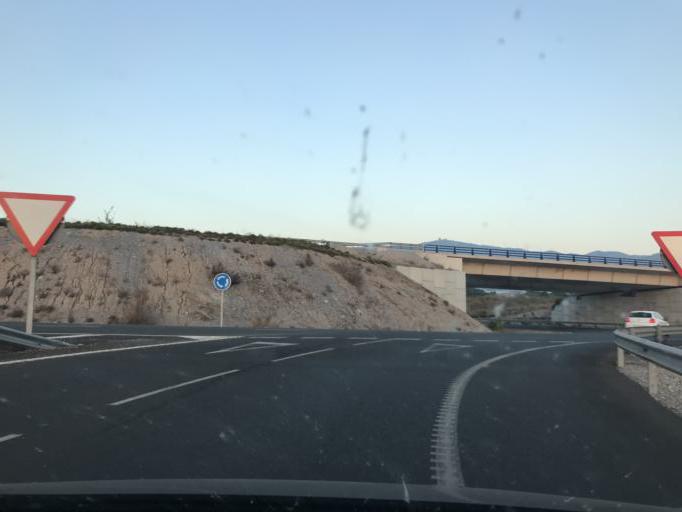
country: ES
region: Andalusia
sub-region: Provincia de Granada
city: Motril
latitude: 36.7388
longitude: -3.4866
